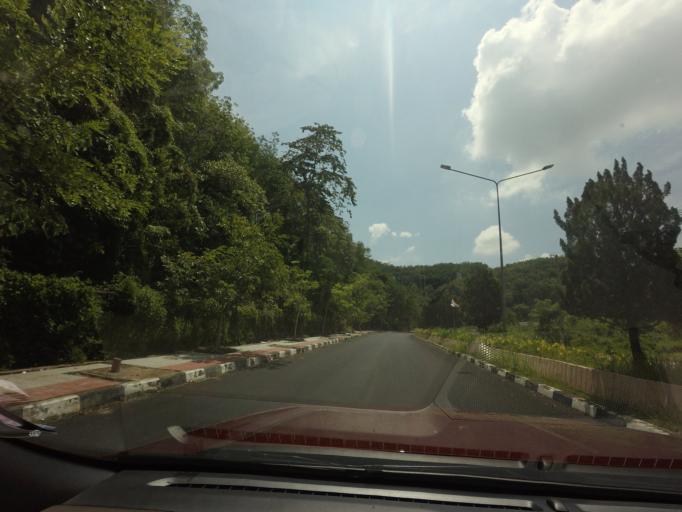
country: TH
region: Yala
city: Betong
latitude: 5.7631
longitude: 101.0475
